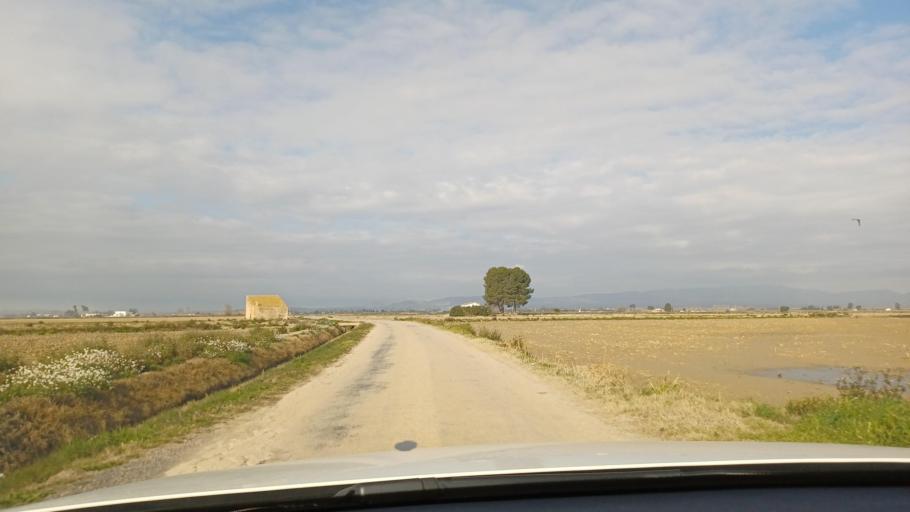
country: ES
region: Catalonia
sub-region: Provincia de Tarragona
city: Deltebre
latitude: 40.6951
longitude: 0.6499
